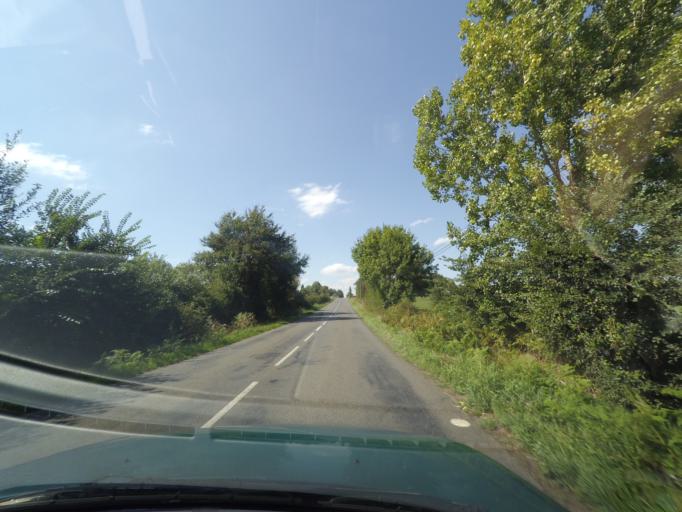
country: FR
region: Pays de la Loire
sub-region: Departement de la Loire-Atlantique
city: Saint-Lumine-de-Coutais
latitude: 47.0409
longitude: -1.7106
